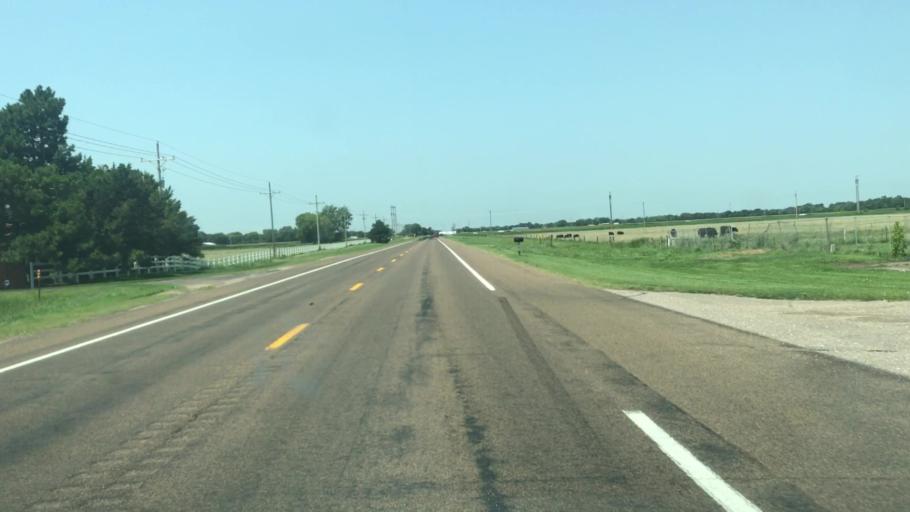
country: US
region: Nebraska
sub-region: Hall County
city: Grand Island
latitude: 40.8869
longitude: -98.3108
